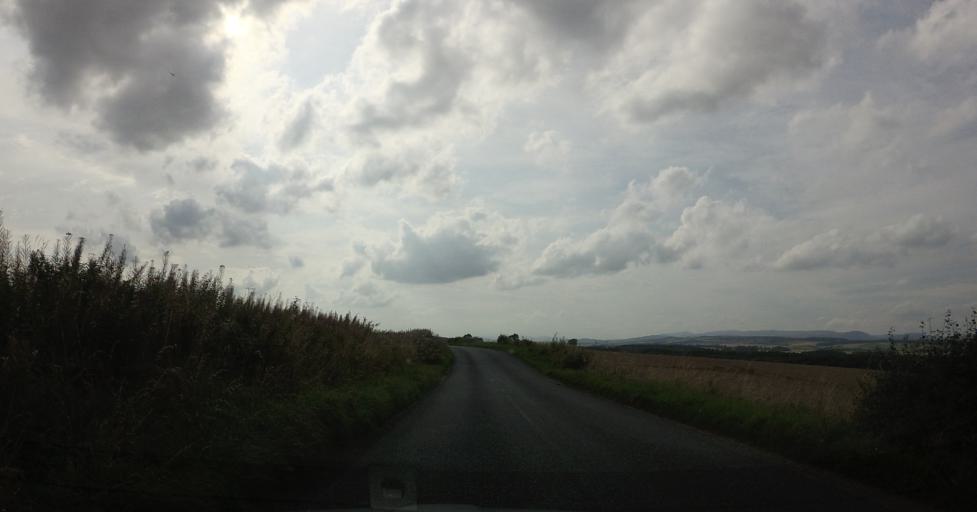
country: GB
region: Scotland
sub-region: Perth and Kinross
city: Methven
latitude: 56.3914
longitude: -3.5797
